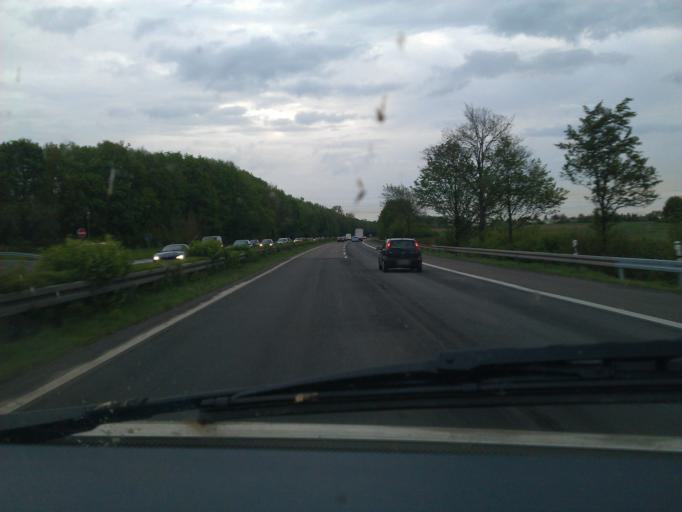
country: DE
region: North Rhine-Westphalia
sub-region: Regierungsbezirk Koln
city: Alsdorf
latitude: 50.8456
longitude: 6.1956
